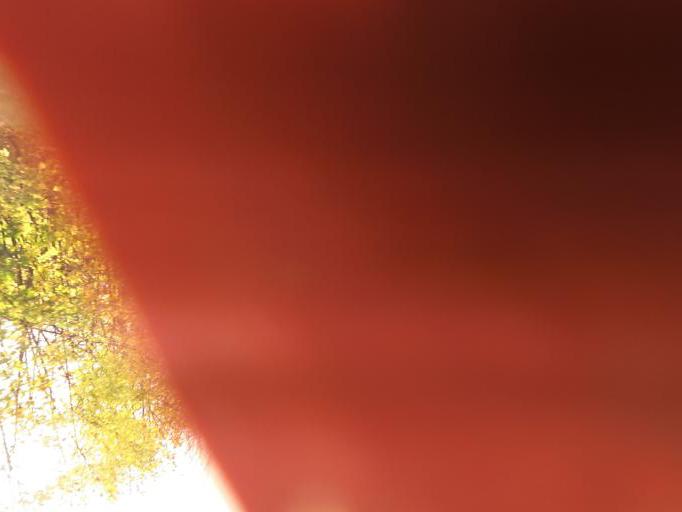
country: DE
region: Saxony-Anhalt
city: Osterfeld
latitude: 51.0778
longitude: 11.9827
